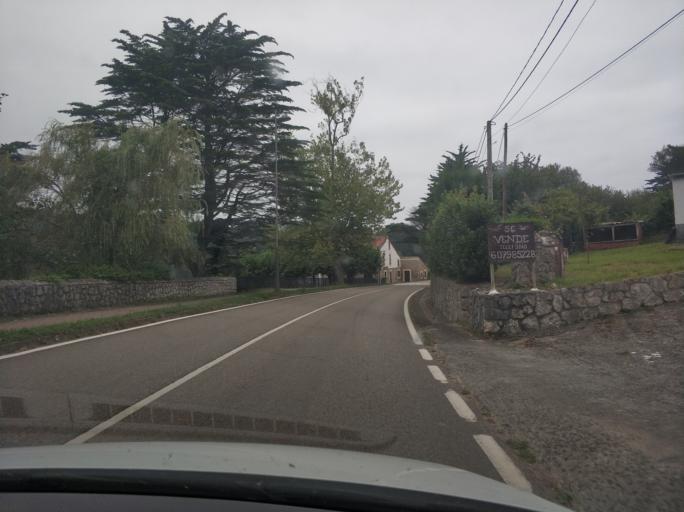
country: ES
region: Cantabria
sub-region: Provincia de Cantabria
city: Comillas
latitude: 43.3791
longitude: -4.3165
